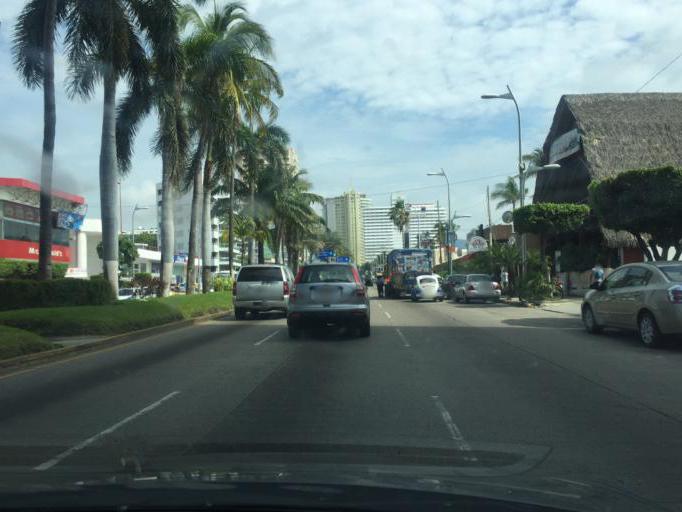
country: MX
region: Guerrero
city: Acapulco de Juarez
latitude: 16.8584
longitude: -99.8708
